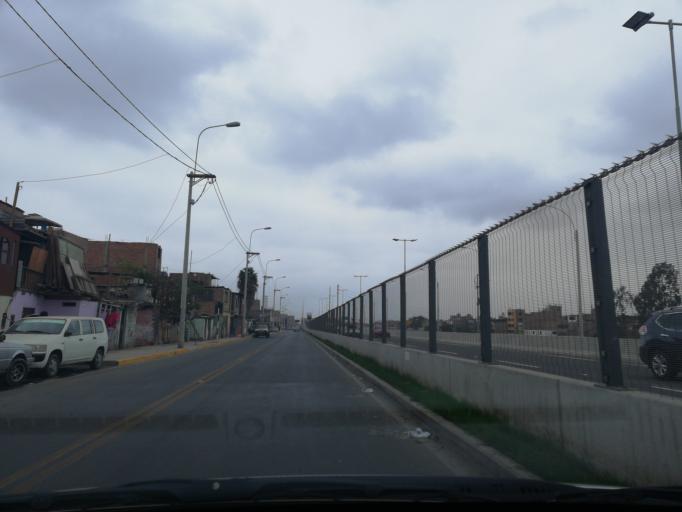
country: PE
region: Lima
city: Lima
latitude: -12.0357
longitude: -77.0621
